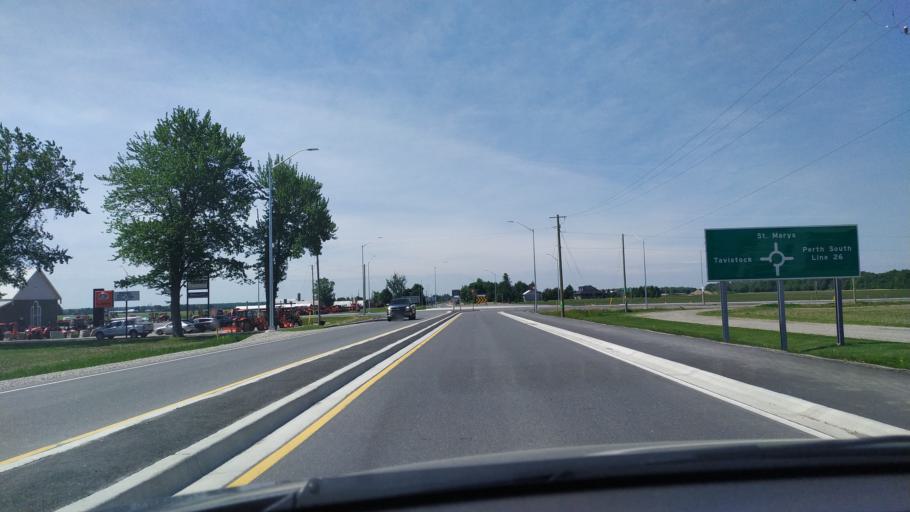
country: CA
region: Ontario
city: Stratford
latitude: 43.3254
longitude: -81.0217
